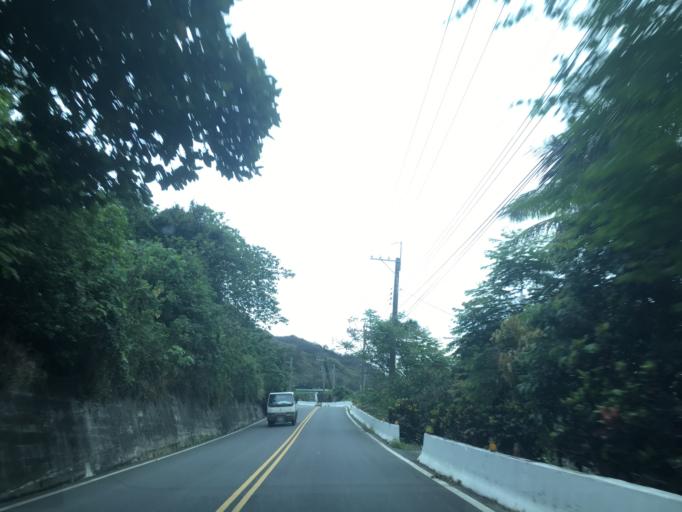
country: TW
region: Taiwan
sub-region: Taitung
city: Taitung
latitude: 22.8180
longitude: 121.1365
